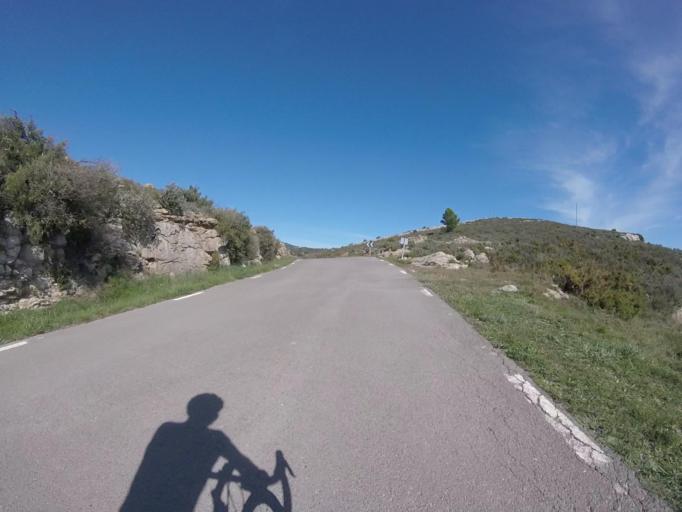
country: ES
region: Valencia
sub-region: Provincia de Castello
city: Sarratella
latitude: 40.2924
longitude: 0.0313
